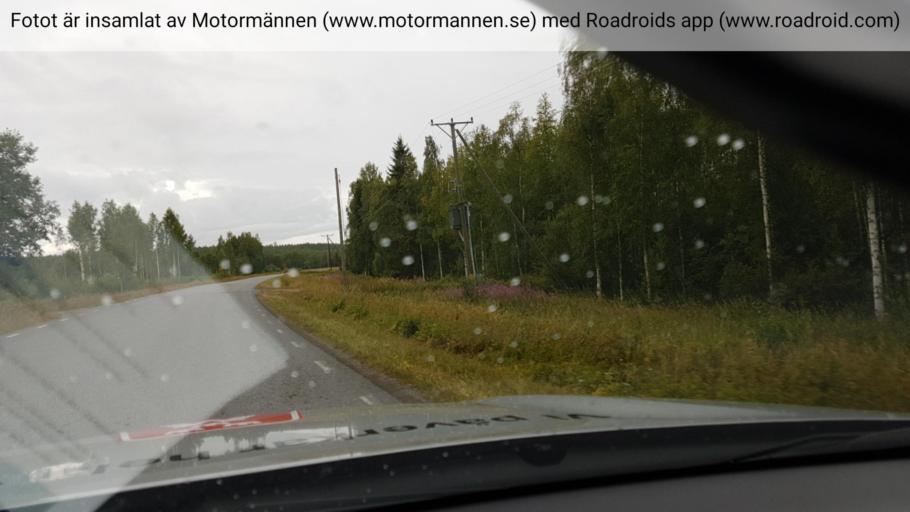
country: SE
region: Norrbotten
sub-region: Bodens Kommun
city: Boden
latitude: 65.8240
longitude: 21.5309
